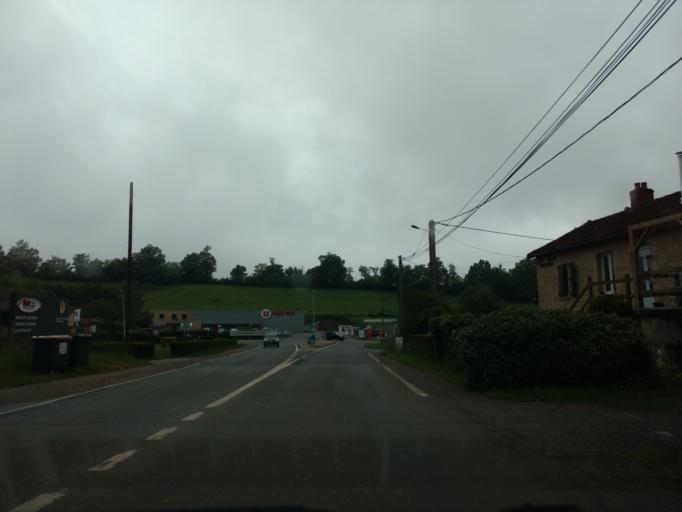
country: FR
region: Midi-Pyrenees
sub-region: Departement de l'Aveyron
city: Montbazens
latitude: 44.4607
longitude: 2.2236
